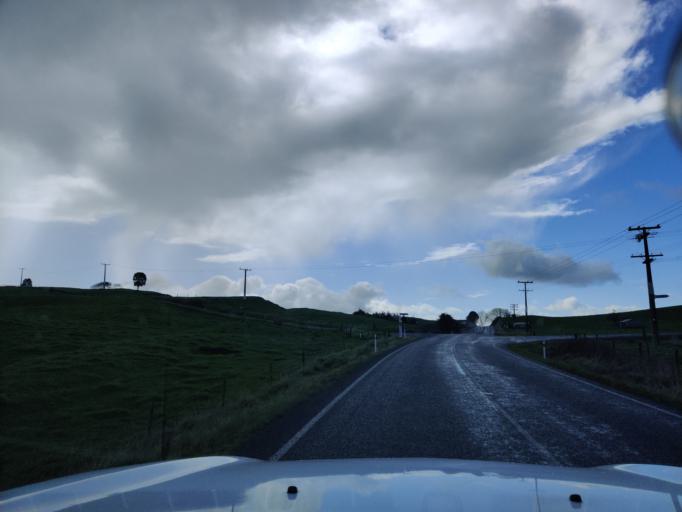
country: NZ
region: Waikato
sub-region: Waikato District
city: Ngaruawahia
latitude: -37.5776
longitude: 175.2293
